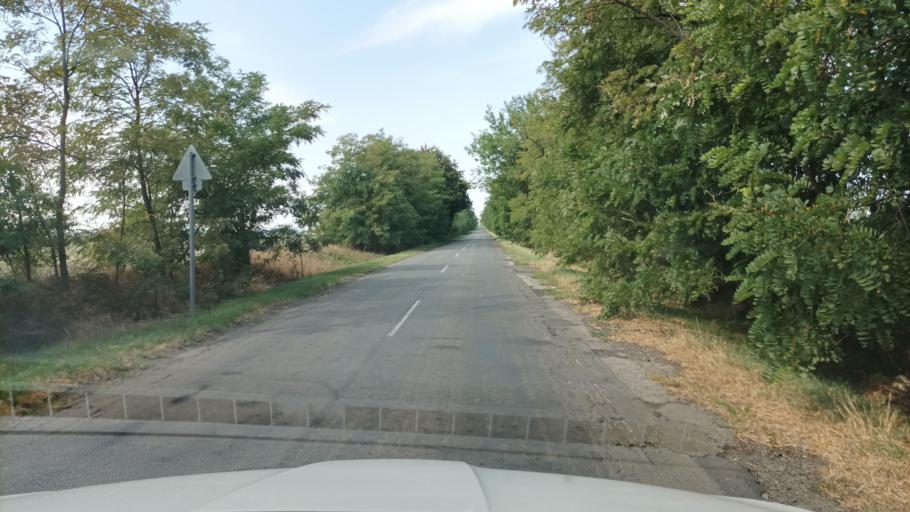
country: HU
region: Heves
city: Boldog
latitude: 47.6124
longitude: 19.6557
